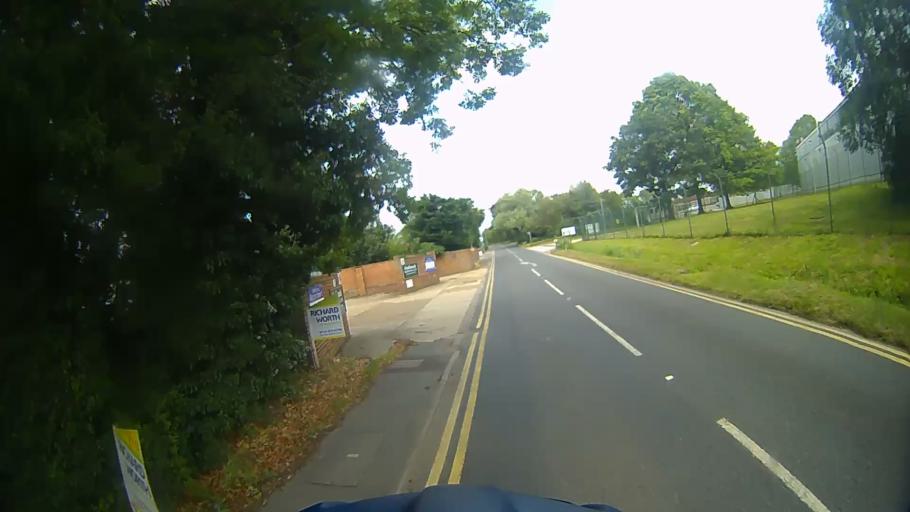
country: GB
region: England
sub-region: Wokingham
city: Barkham
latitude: 51.3916
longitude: -0.8970
